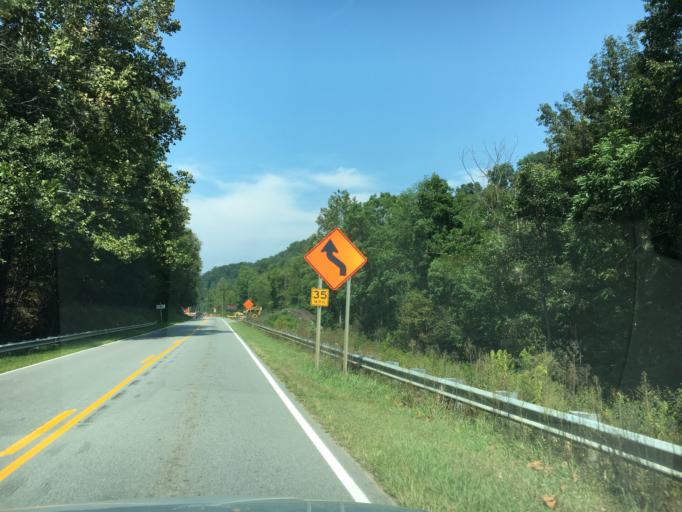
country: US
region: North Carolina
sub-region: McDowell County
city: West Marion
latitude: 35.5682
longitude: -81.9718
